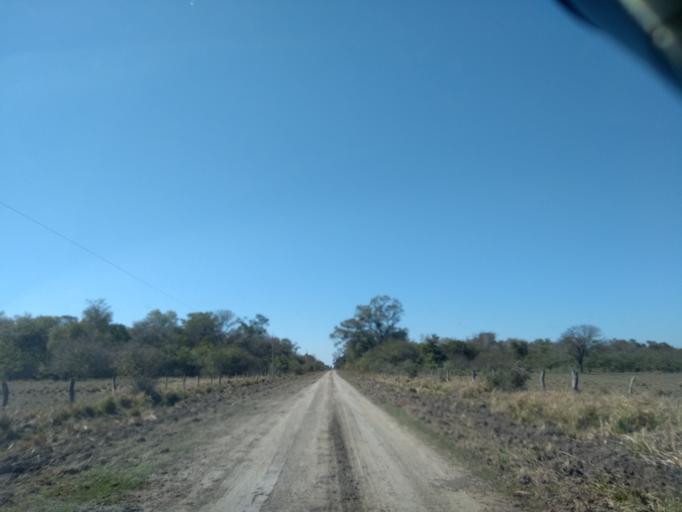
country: AR
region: Chaco
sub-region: Departamento de Quitilipi
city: Quitilipi
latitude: -26.7086
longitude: -60.2153
